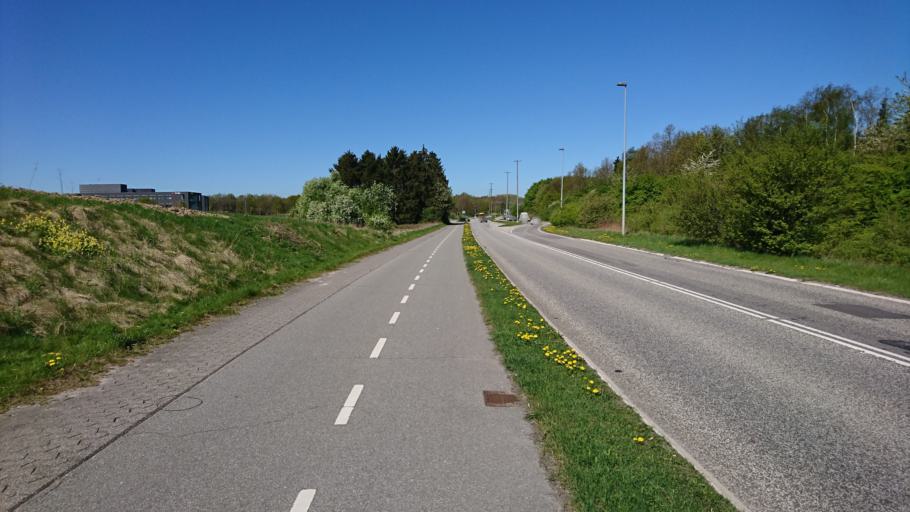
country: DK
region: Capital Region
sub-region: Ballerup Kommune
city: Ballerup
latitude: 55.7410
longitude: 12.3956
